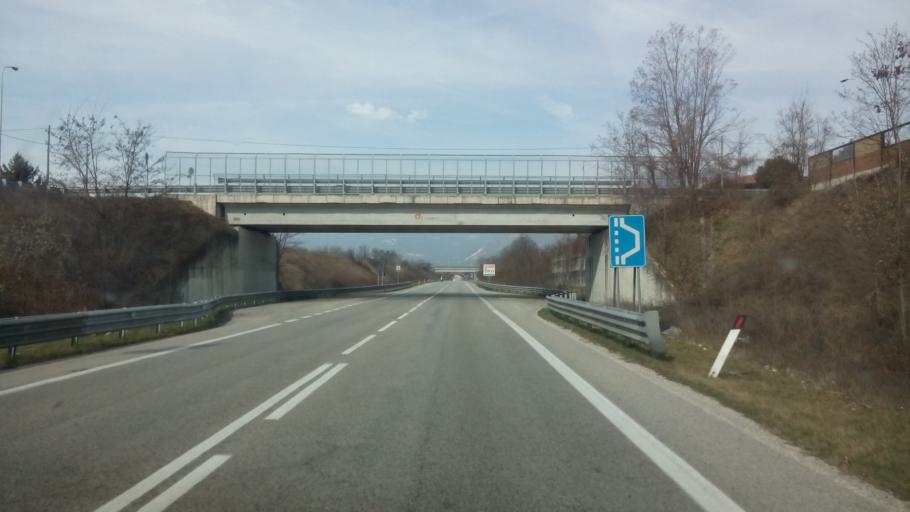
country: IT
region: Veneto
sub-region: Provincia di Vicenza
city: Zane
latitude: 45.7066
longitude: 11.4501
